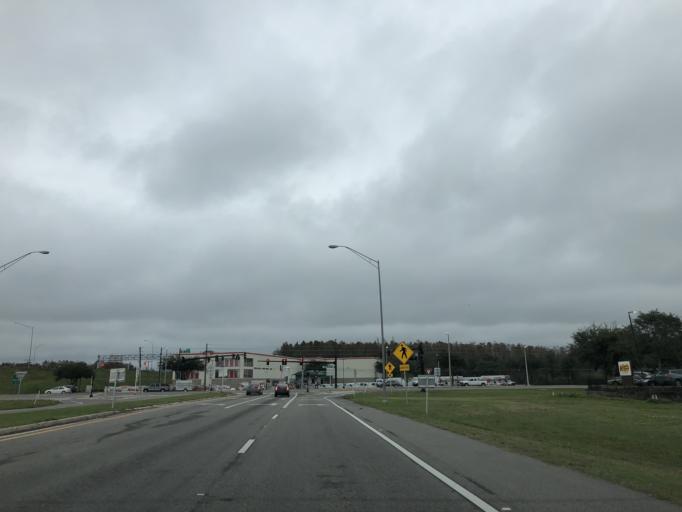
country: US
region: Florida
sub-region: Orange County
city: Hunters Creek
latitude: 28.3715
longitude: -81.4057
